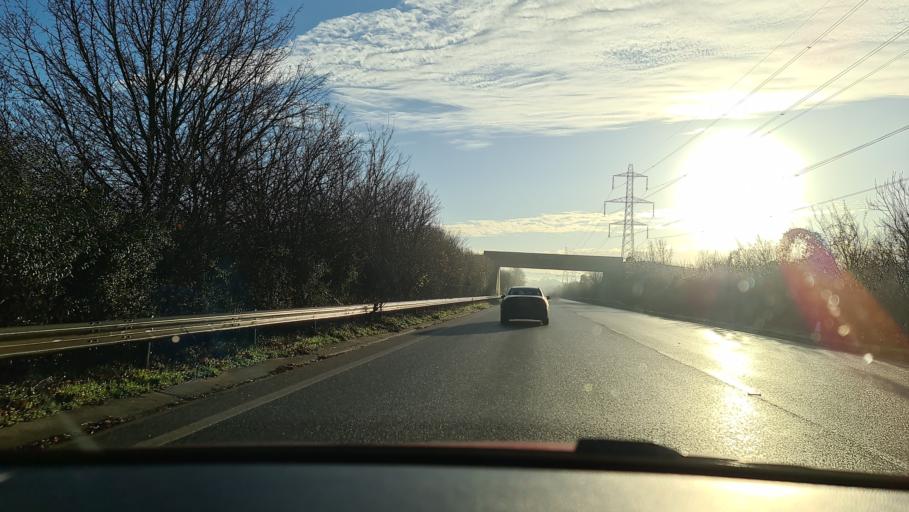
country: GB
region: England
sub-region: Buckinghamshire
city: Wendover
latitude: 51.7656
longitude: -0.7558
